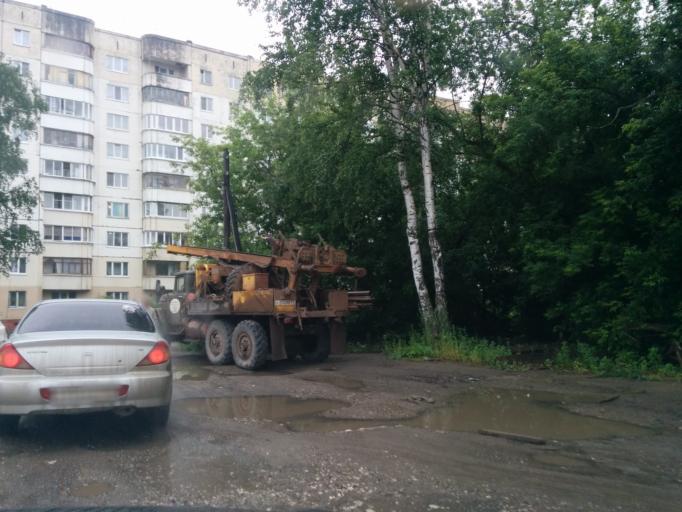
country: RU
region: Perm
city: Kondratovo
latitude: 58.0374
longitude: 56.0337
